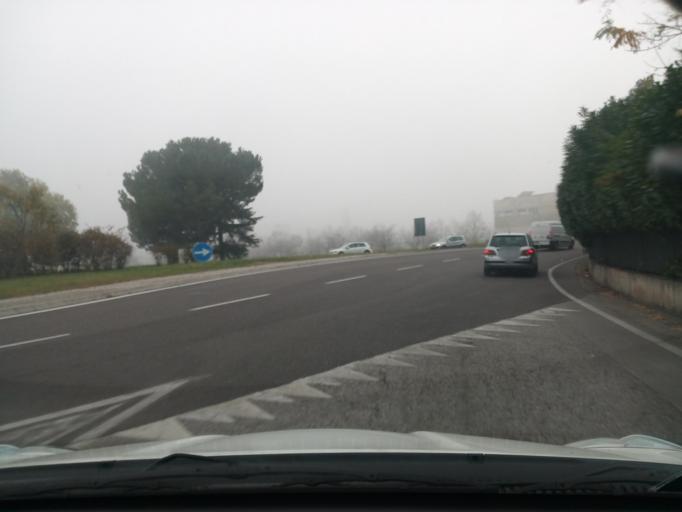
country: IT
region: Veneto
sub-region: Provincia di Vicenza
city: Santorso
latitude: 45.7171
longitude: 11.3875
